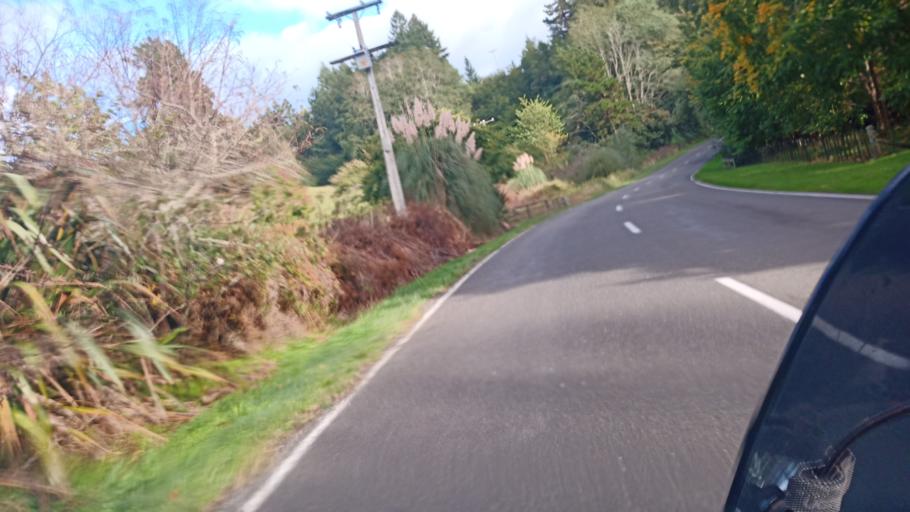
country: NZ
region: Gisborne
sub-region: Gisborne District
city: Gisborne
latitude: -38.5634
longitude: 177.7151
